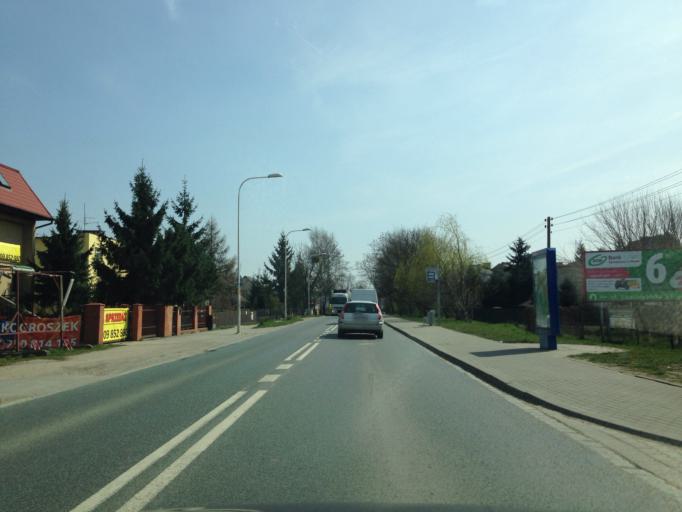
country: PL
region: Lower Silesian Voivodeship
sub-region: Powiat wroclawski
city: Wilczyce
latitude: 51.1091
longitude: 17.1391
